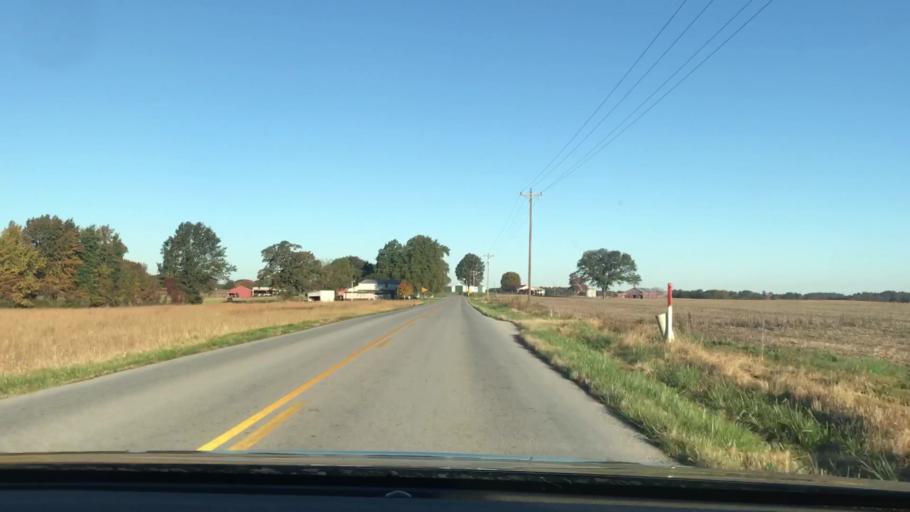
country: US
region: Kentucky
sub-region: Simpson County
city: Franklin
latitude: 36.7603
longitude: -86.6058
